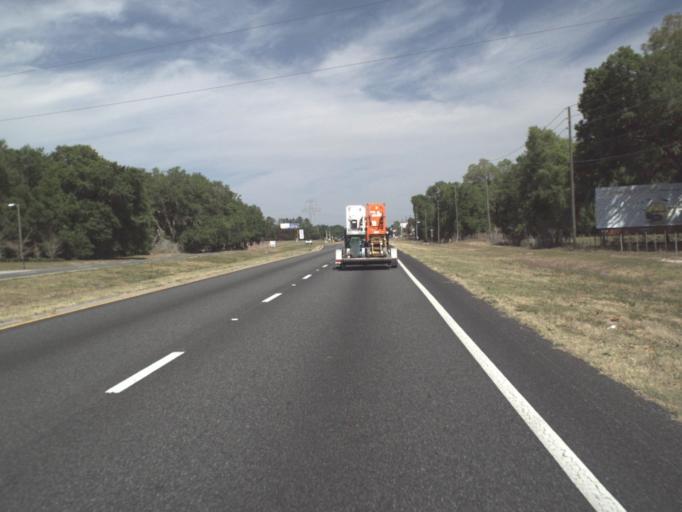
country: US
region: Florida
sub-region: Marion County
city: Belleview
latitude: 29.0239
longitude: -82.0179
